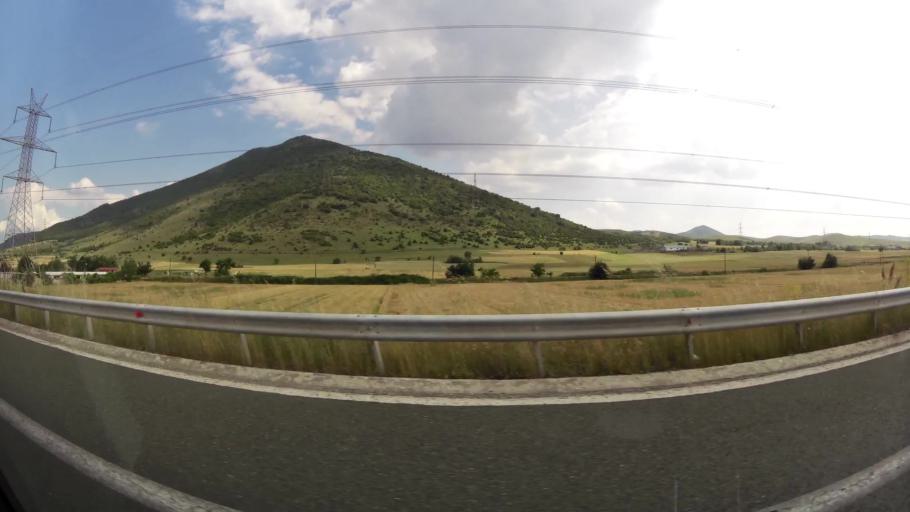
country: GR
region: West Macedonia
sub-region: Nomos Kozanis
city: Kleitos
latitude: 40.3698
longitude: 21.8858
